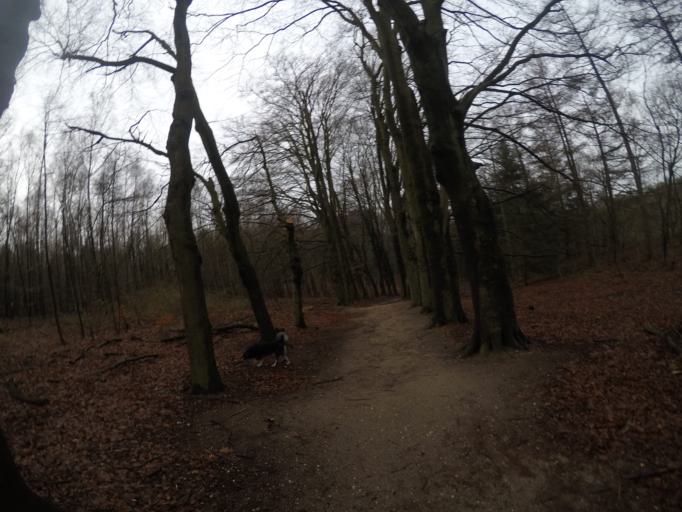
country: NL
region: Gelderland
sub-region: Gemeente Arnhem
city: Hoogkamp
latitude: 51.9908
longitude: 5.8719
